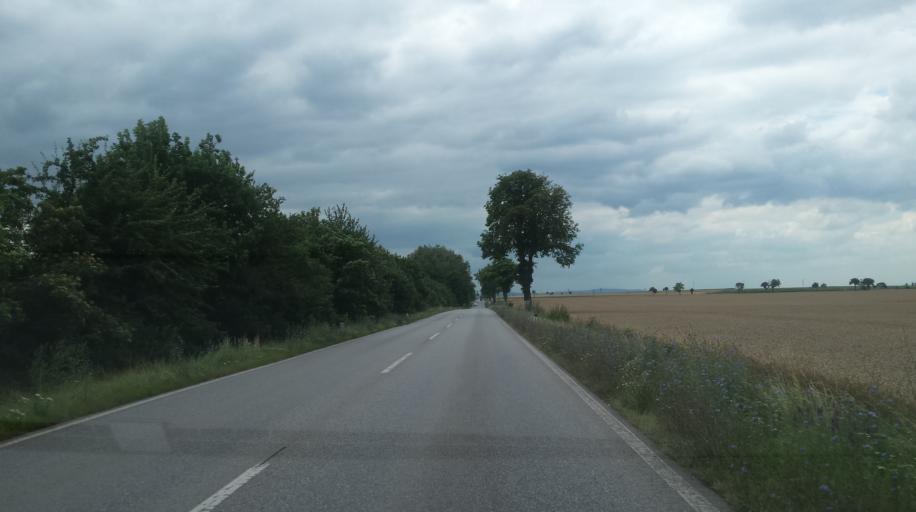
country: AT
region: Lower Austria
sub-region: Politischer Bezirk Wien-Umgebung
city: Himberg
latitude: 48.0574
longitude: 16.4594
